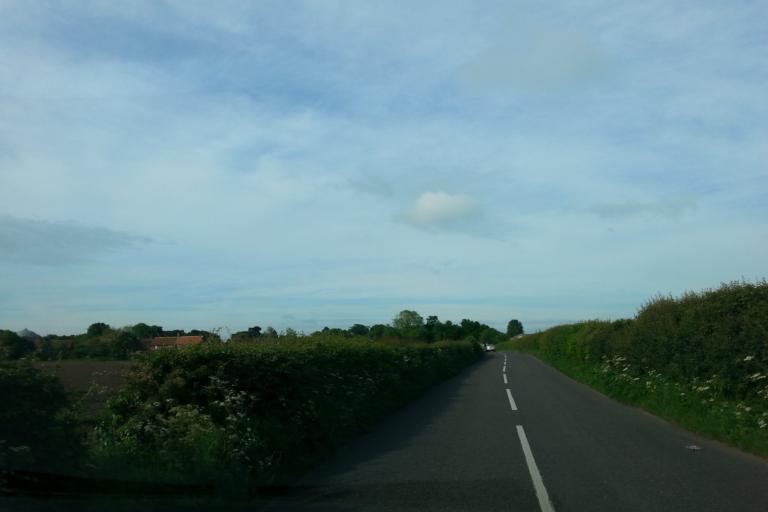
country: GB
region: England
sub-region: Nottinghamshire
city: Newark on Trent
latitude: 53.0963
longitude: -0.8440
